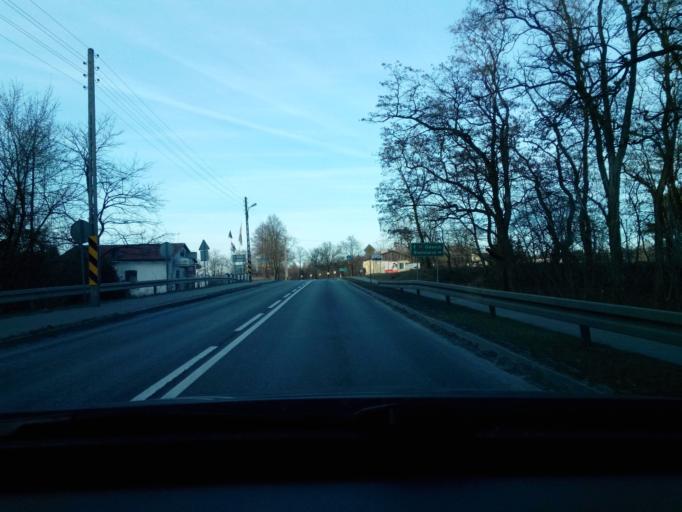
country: PL
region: Kujawsko-Pomorskie
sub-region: Powiat wloclawski
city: Lubien Kujawski
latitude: 52.4087
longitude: 19.1659
